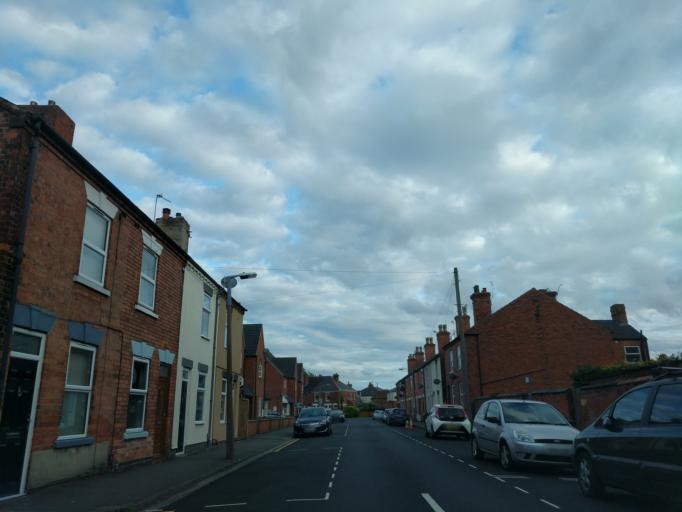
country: GB
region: England
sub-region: Nottinghamshire
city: Newark on Trent
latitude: 53.0806
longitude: -0.8013
